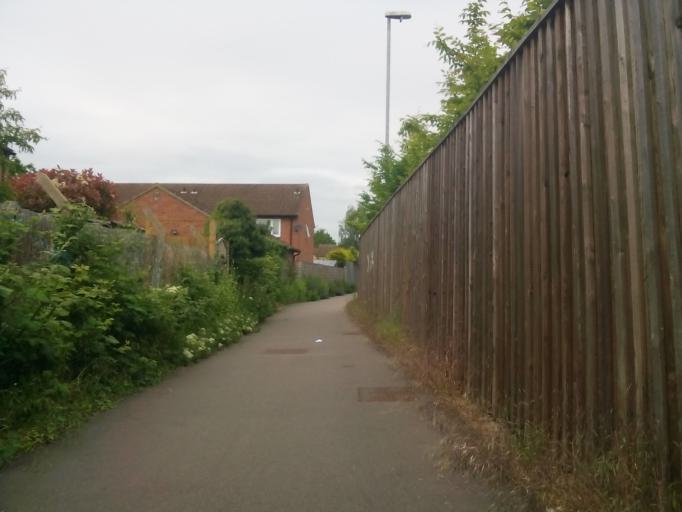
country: GB
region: England
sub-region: Cambridgeshire
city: Histon
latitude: 52.2423
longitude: 0.1099
